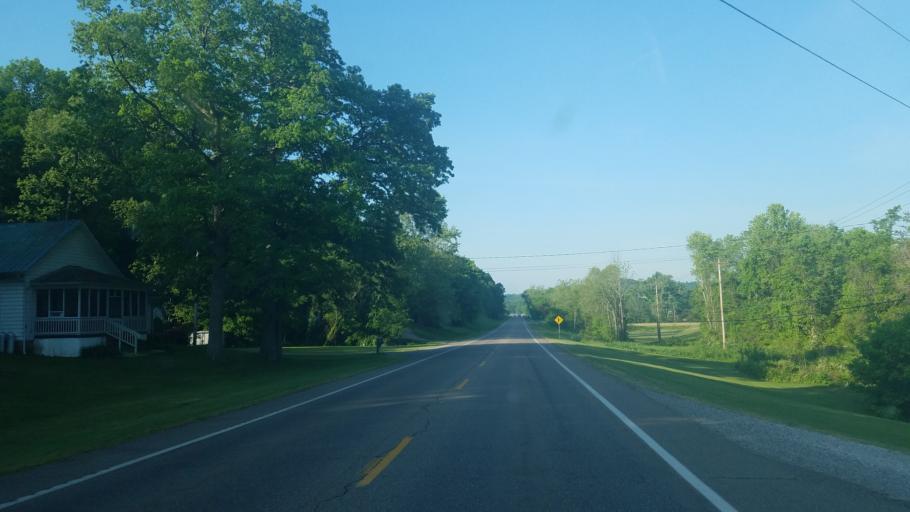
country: US
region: West Virginia
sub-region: Mason County
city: New Haven
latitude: 39.1106
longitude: -81.9186
